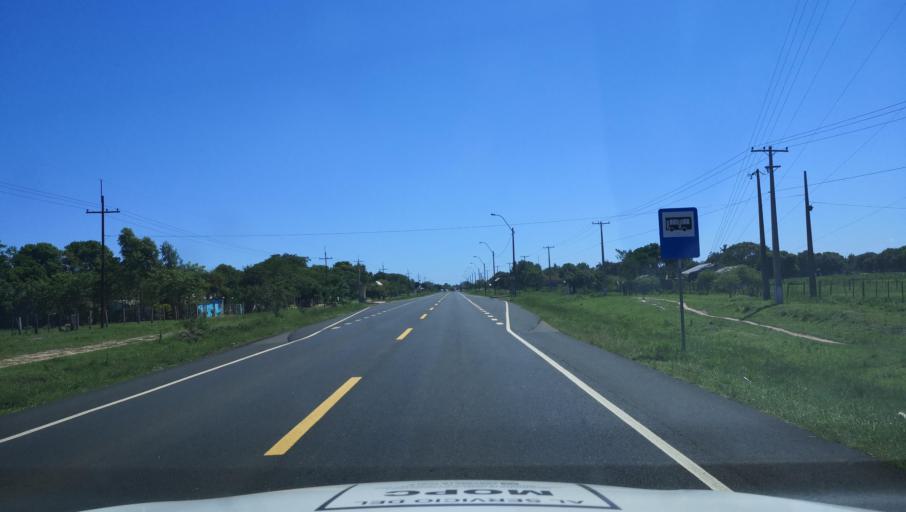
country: PY
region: Caaguazu
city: Carayao
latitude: -25.2088
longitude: -56.3984
